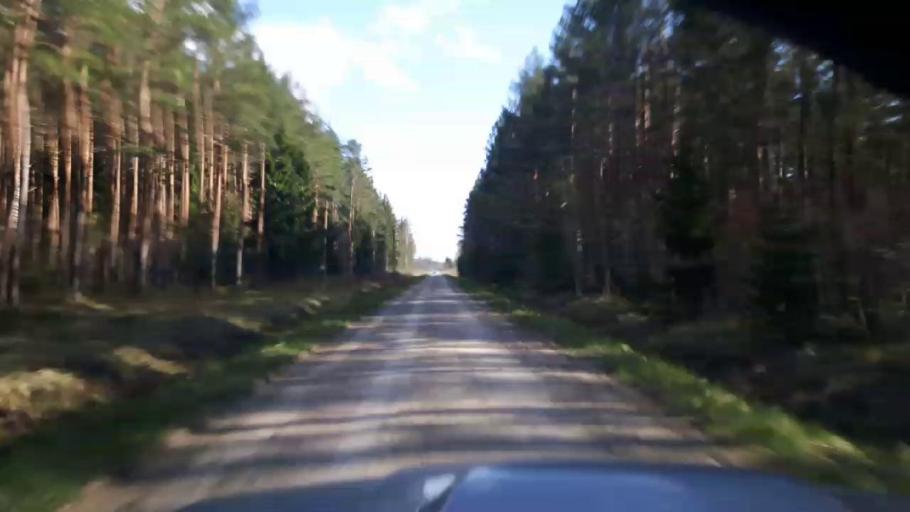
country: EE
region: Paernumaa
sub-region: Tootsi vald
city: Tootsi
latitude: 58.4217
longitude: 24.8517
